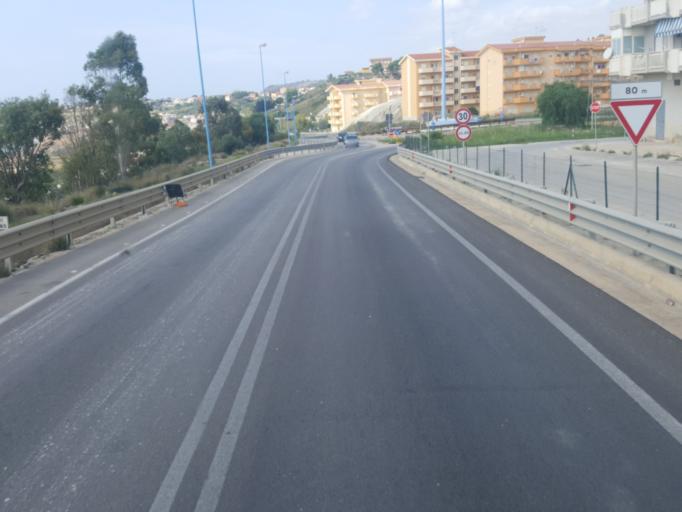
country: IT
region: Sicily
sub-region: Agrigento
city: Porto Empedocle
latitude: 37.2926
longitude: 13.5141
